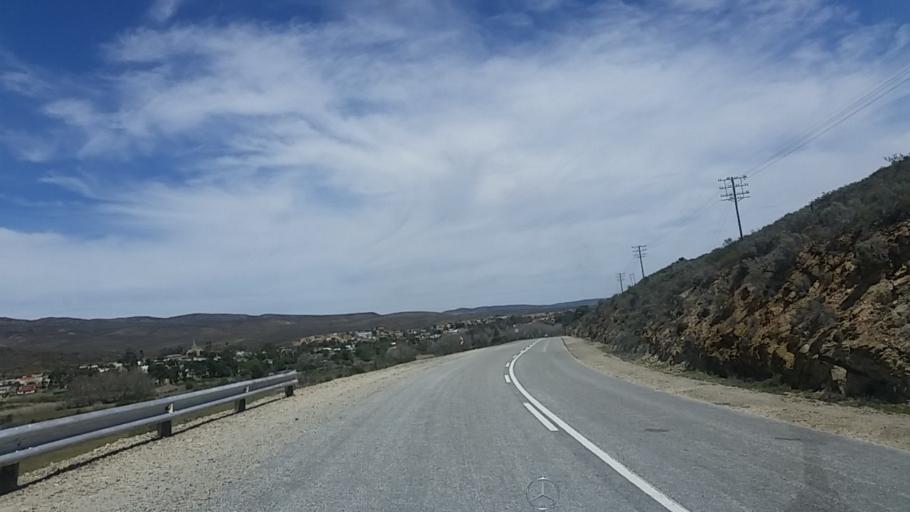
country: ZA
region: Western Cape
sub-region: Eden District Municipality
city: Knysna
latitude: -33.6463
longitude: 23.1324
